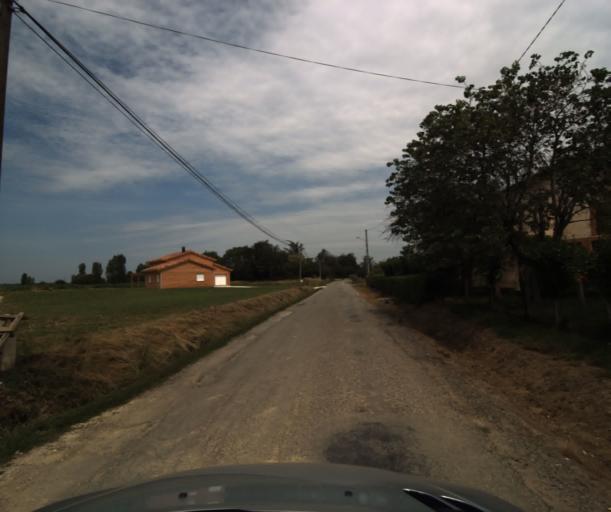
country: FR
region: Midi-Pyrenees
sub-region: Departement de la Haute-Garonne
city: Lacasse
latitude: 43.4158
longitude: 1.2714
